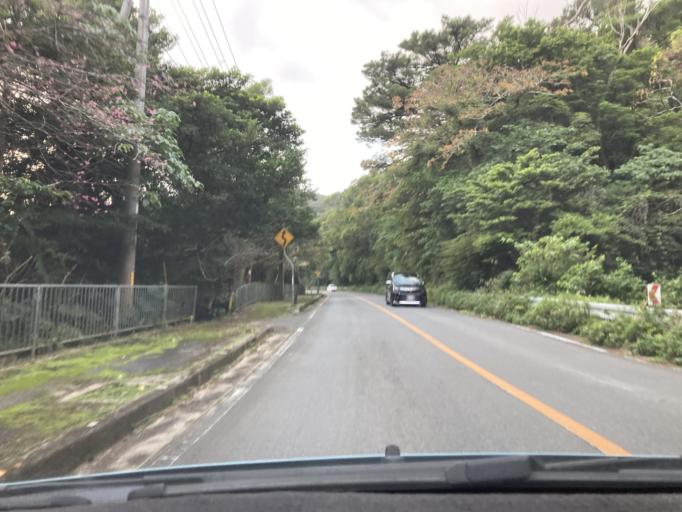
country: JP
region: Okinawa
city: Nago
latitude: 26.8323
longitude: 128.2819
